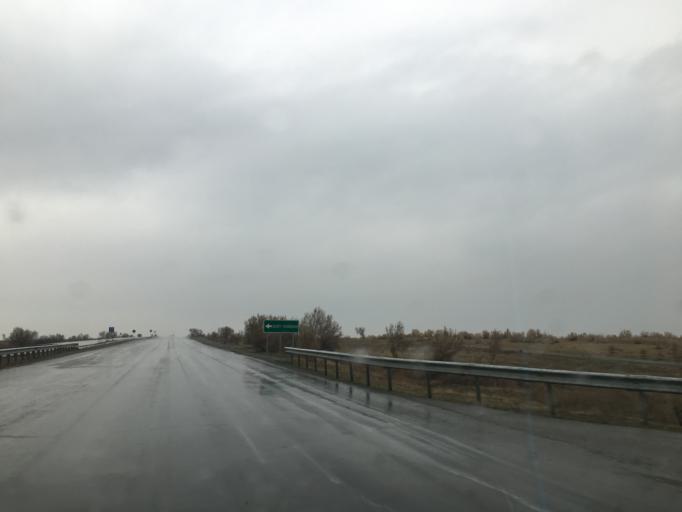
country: TM
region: Ahal
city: Annau
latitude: 37.8549
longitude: 58.6907
